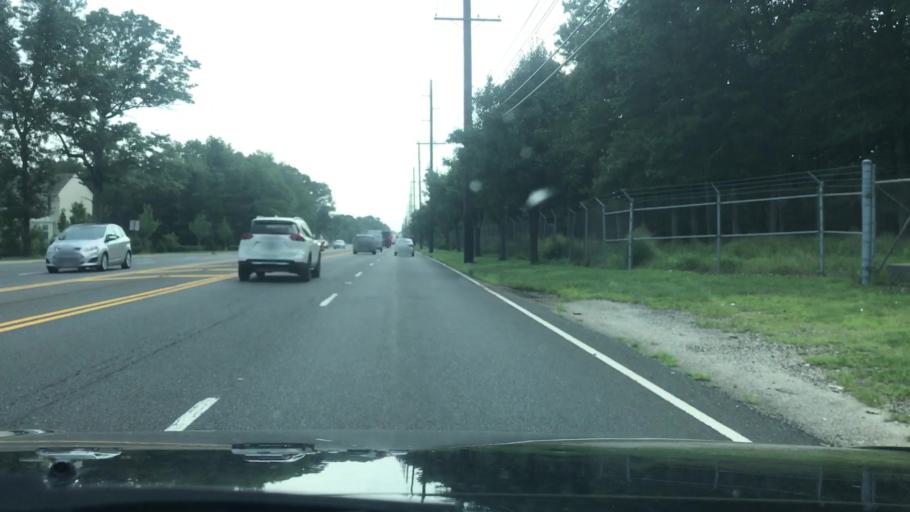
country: US
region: New Jersey
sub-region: Monmouth County
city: Tinton Falls
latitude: 40.2611
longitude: -74.0895
